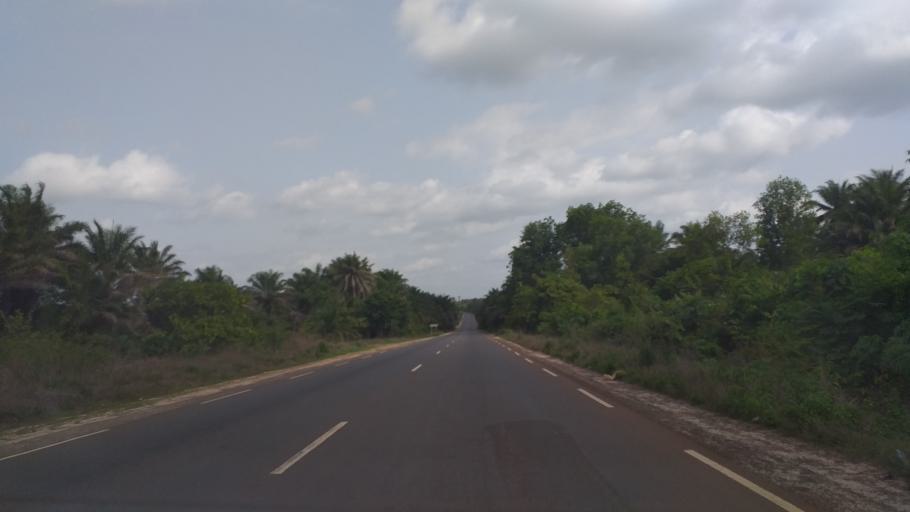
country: GN
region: Boke
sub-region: Boke Prefecture
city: Sangueya
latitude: 10.7384
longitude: -14.3790
